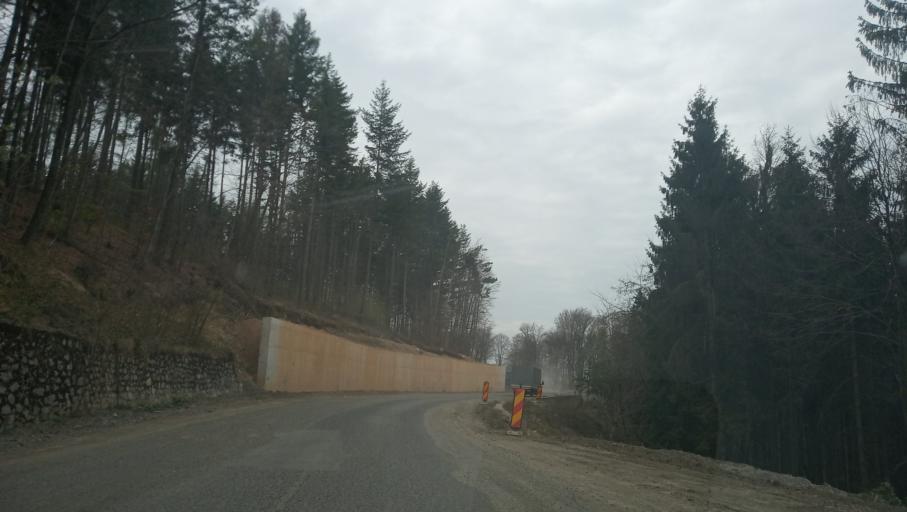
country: RO
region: Bihor
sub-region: Comuna Cristioru de Jos
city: Cristioru de Jos
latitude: 46.3936
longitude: 22.5534
